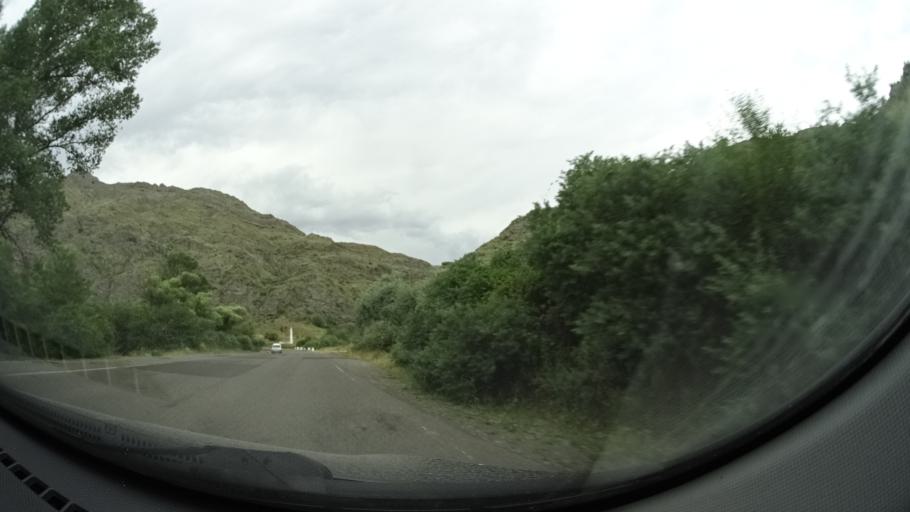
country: GE
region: Samtskhe-Javakheti
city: Akhaltsikhe
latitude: 41.6166
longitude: 43.1045
